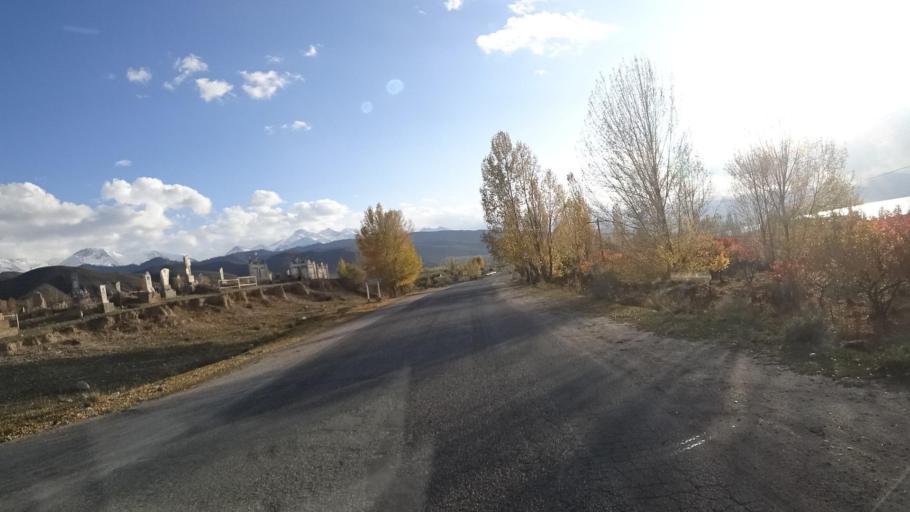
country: KG
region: Ysyk-Koel
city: Pokrovka
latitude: 42.2271
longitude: 77.7138
